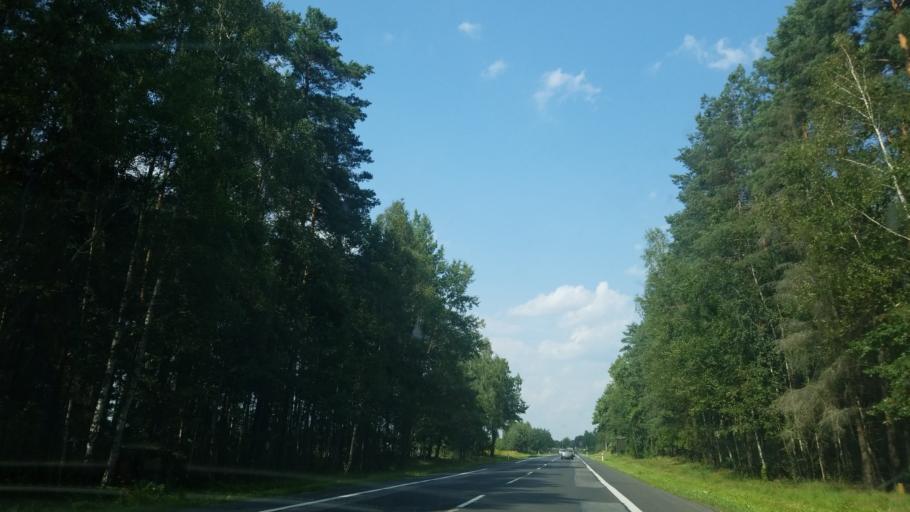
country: PL
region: Subcarpathian Voivodeship
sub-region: Powiat nizanski
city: Jarocin
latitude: 50.5868
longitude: 22.2766
